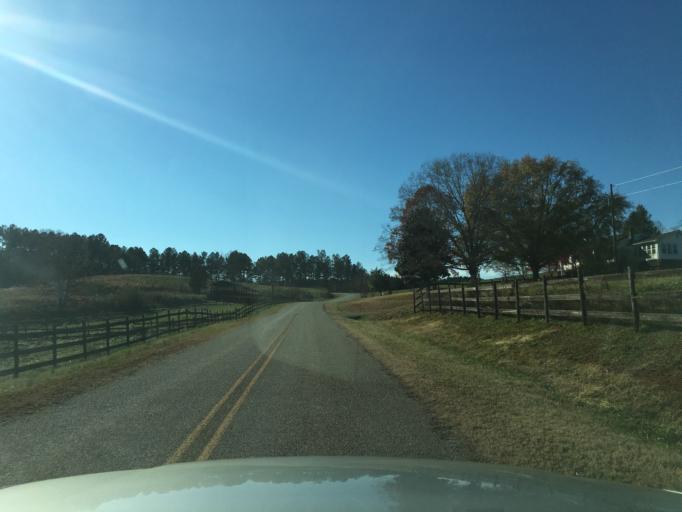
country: US
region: North Carolina
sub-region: Rutherford County
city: Rutherfordton
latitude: 35.2544
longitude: -82.0405
